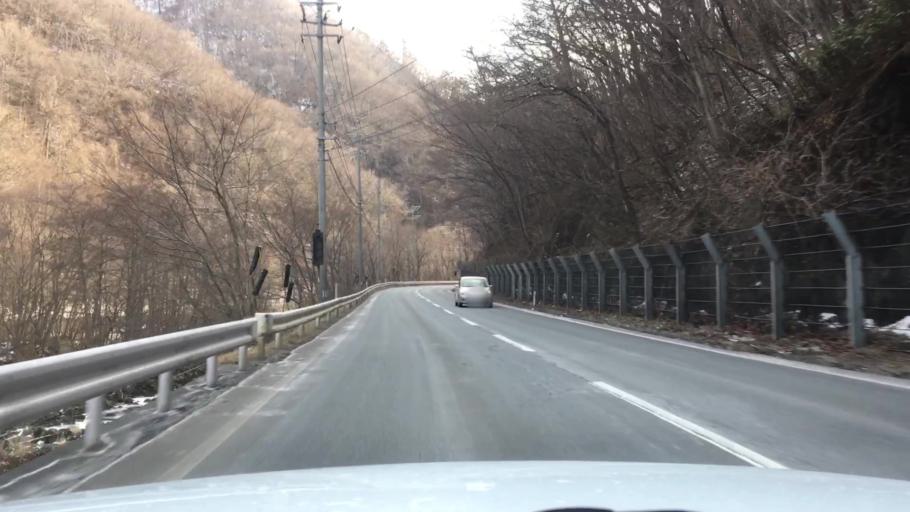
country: JP
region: Iwate
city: Tono
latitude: 39.6374
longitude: 141.5366
